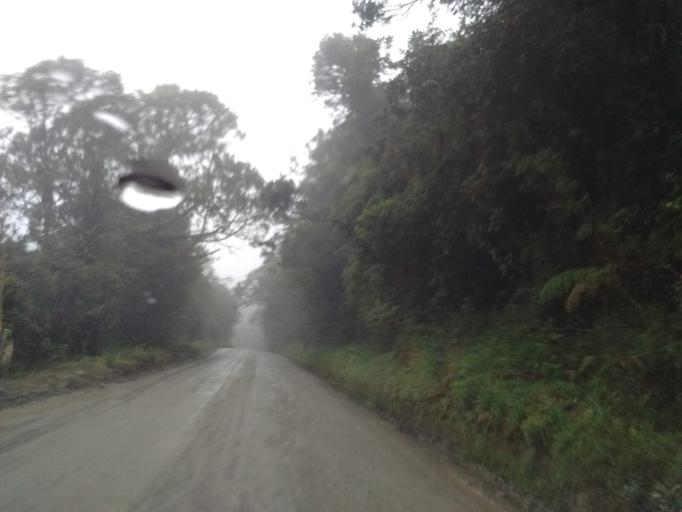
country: CO
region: Cauca
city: Paispamba
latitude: 2.1507
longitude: -76.4485
